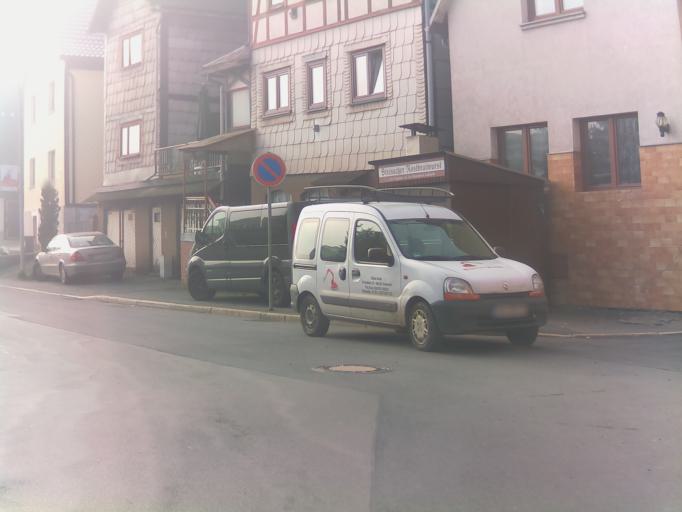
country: DE
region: Thuringia
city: Steinach
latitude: 50.4256
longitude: 11.1630
